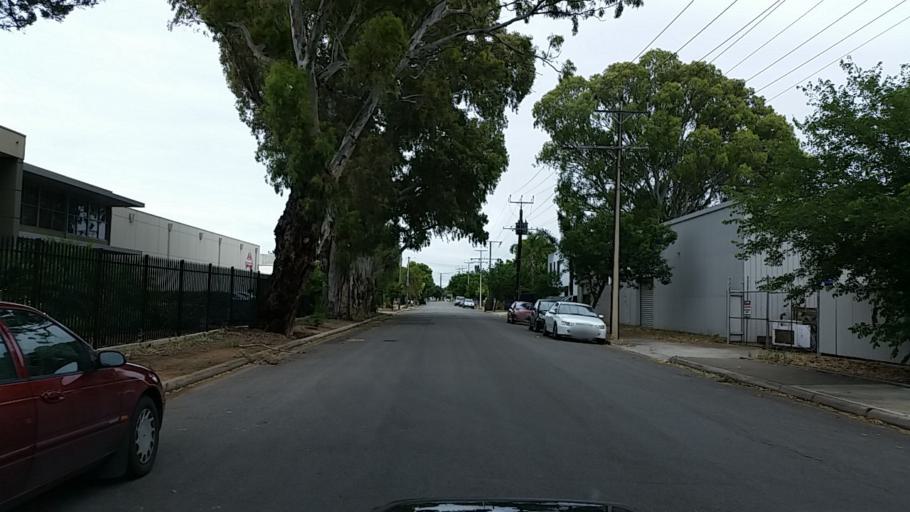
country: AU
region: South Australia
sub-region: Charles Sturt
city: Woodville
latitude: -34.8902
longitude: 138.5436
